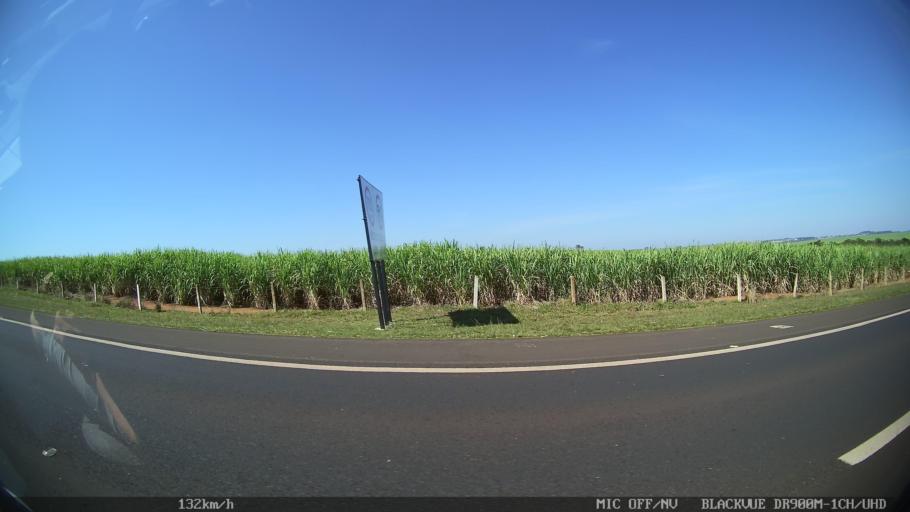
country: BR
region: Sao Paulo
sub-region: Batatais
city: Batatais
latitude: -20.8213
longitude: -47.5895
